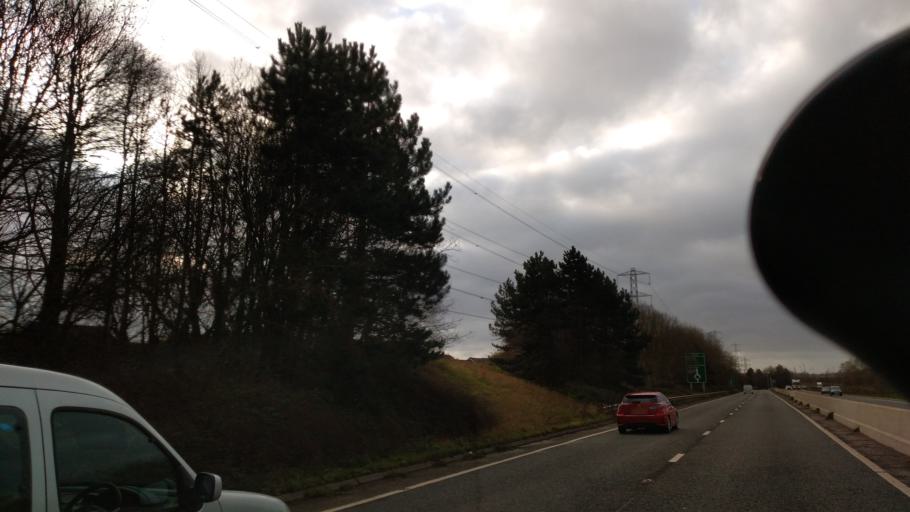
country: GB
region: England
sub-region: Wiltshire
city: Chippenham
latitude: 51.4737
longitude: -2.1378
